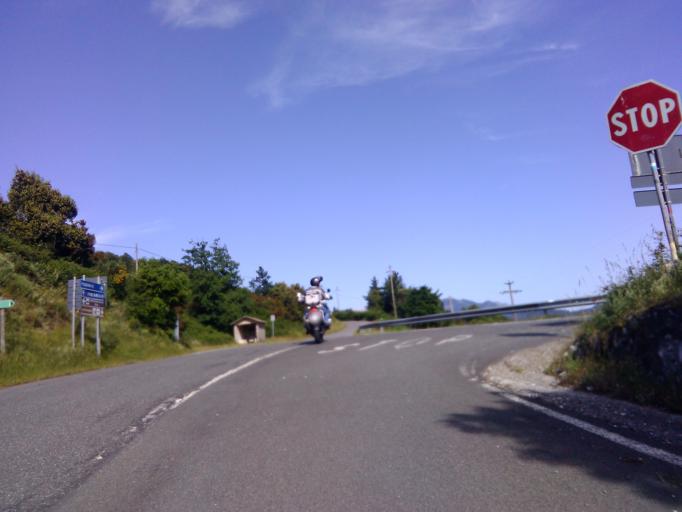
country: IT
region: Tuscany
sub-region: Provincia di Massa-Carrara
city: Fosdinovo
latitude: 44.1580
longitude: 10.0036
